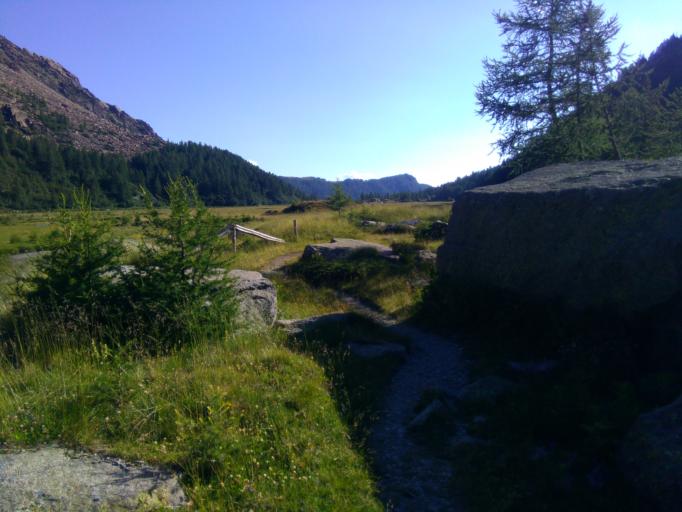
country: IT
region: Lombardy
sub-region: Provincia di Sondrio
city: Buglio in Monte
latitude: 46.2344
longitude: 9.7062
